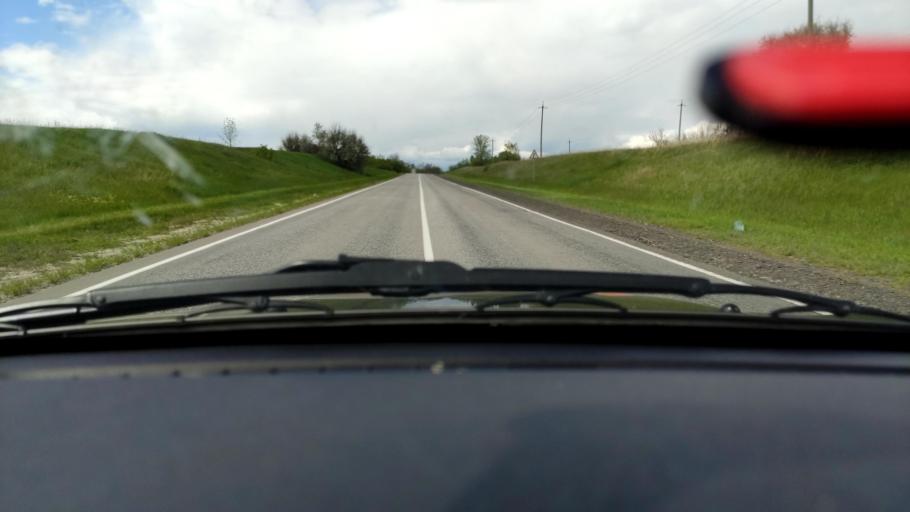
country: RU
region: Voronezj
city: Uryv-Pokrovka
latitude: 51.0728
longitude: 38.9955
